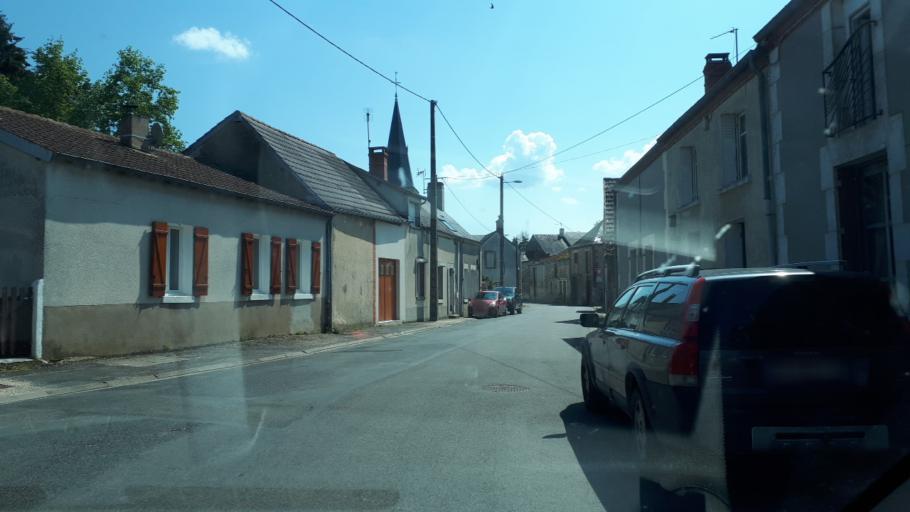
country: FR
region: Centre
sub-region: Departement du Cher
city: Neuvy-sur-Barangeon
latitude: 47.3147
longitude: 2.3612
